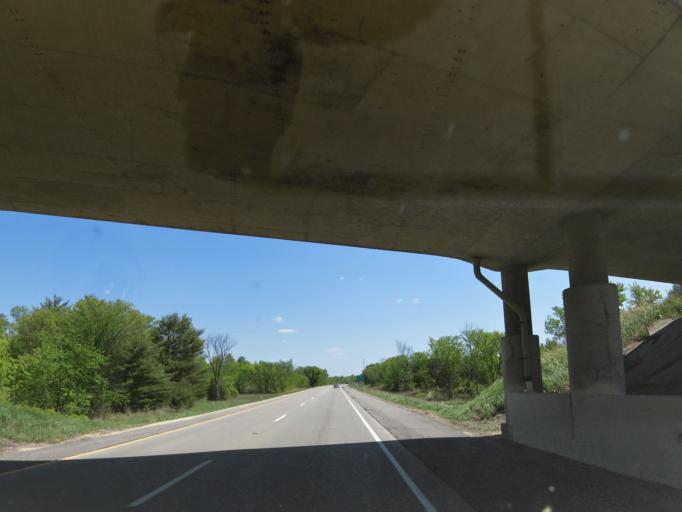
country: US
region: Wisconsin
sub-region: Juneau County
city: New Lisbon
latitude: 43.8943
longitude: -90.1727
